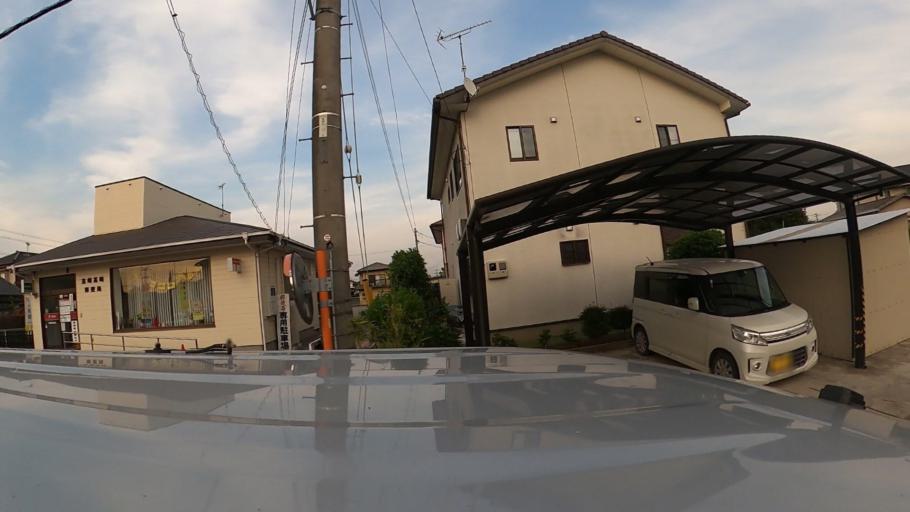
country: JP
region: Ibaraki
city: Ushiku
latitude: 36.0008
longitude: 140.1243
